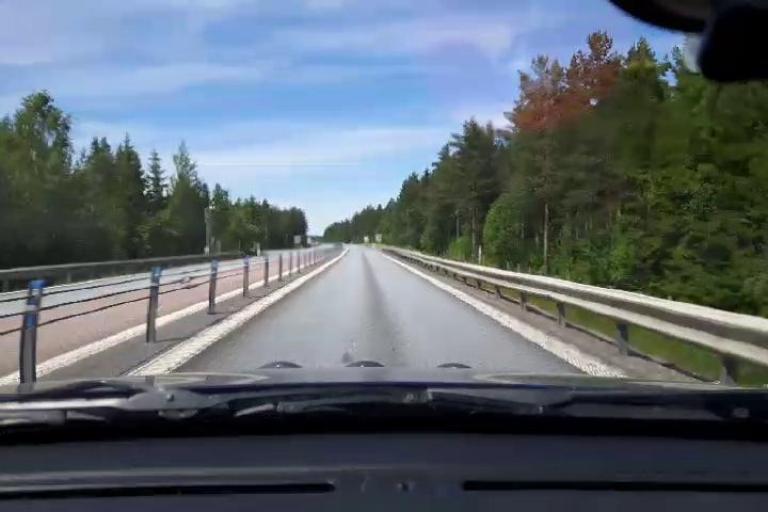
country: SE
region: Gaevleborg
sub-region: Gavle Kommun
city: Gavle
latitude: 60.7443
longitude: 17.0815
